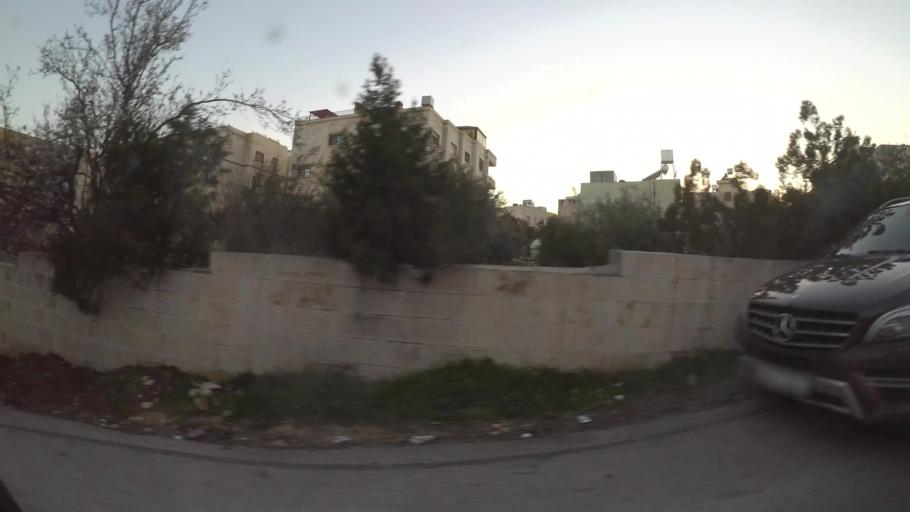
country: JO
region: Amman
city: Al Jubayhah
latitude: 32.0040
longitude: 35.8524
